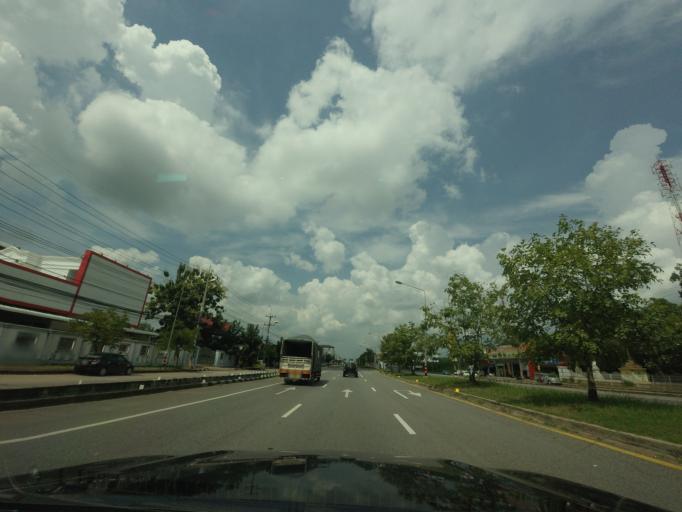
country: TH
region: Khon Kaen
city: Nong Ruea
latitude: 16.4907
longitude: 102.4409
